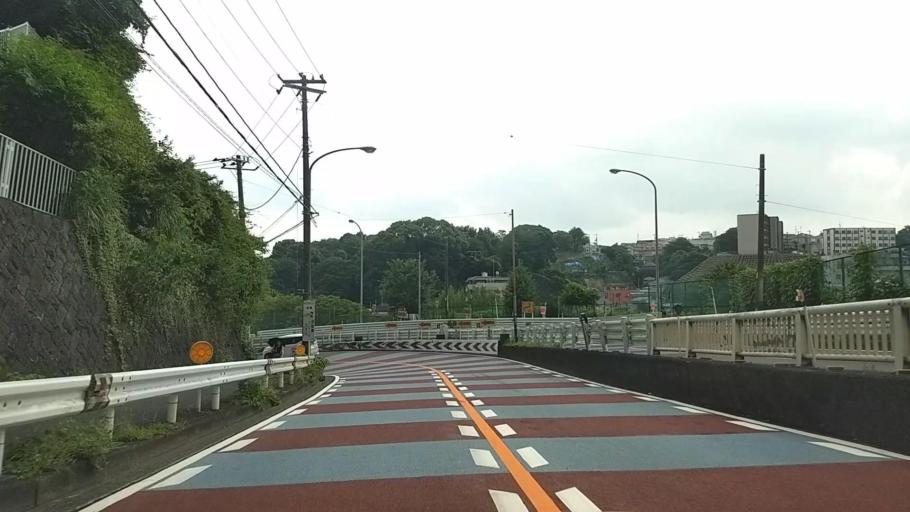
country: JP
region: Kanagawa
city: Yokohama
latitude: 35.4674
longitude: 139.6102
